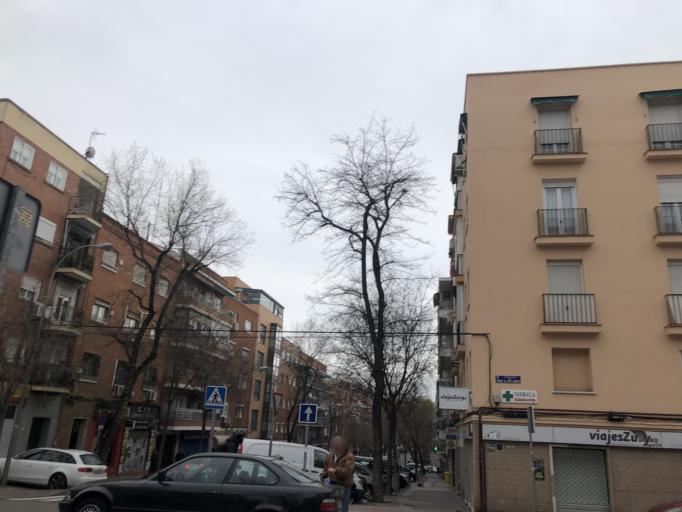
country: ES
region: Madrid
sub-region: Provincia de Madrid
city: Moratalaz
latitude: 40.4335
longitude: -3.6438
